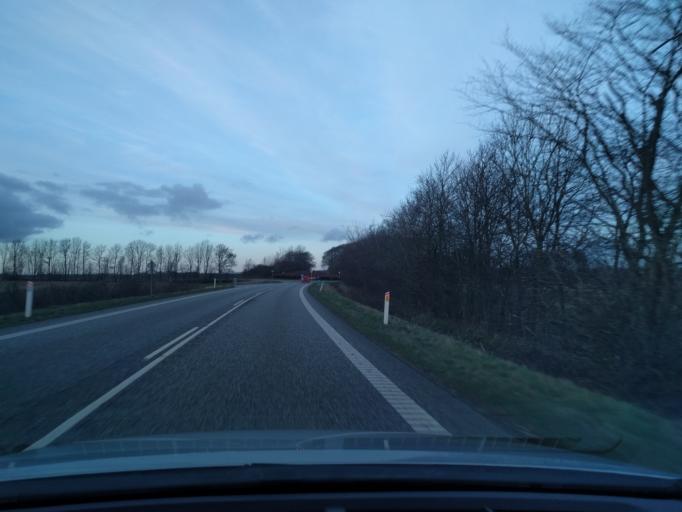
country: DK
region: South Denmark
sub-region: Tonder Kommune
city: Toftlund
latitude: 55.1354
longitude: 9.0044
